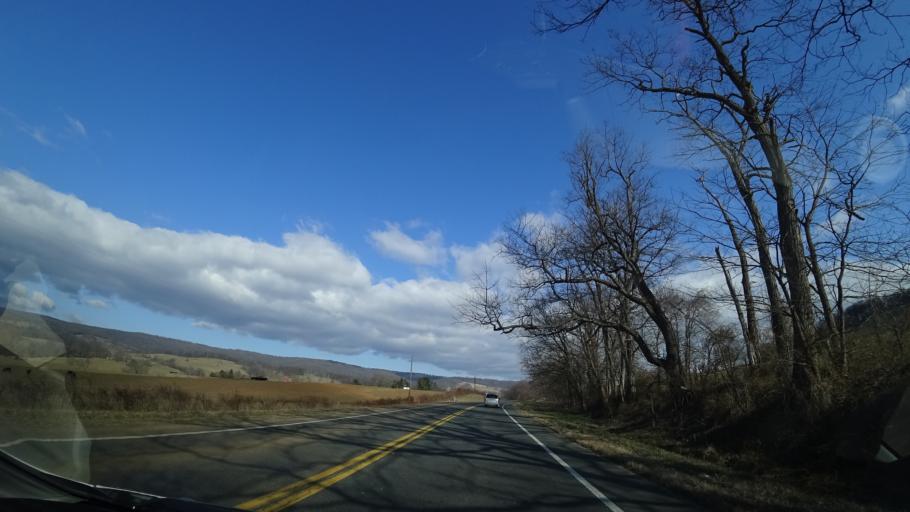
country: US
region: Virginia
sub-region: Warren County
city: Shenandoah Farms
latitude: 38.9702
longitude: -77.9515
